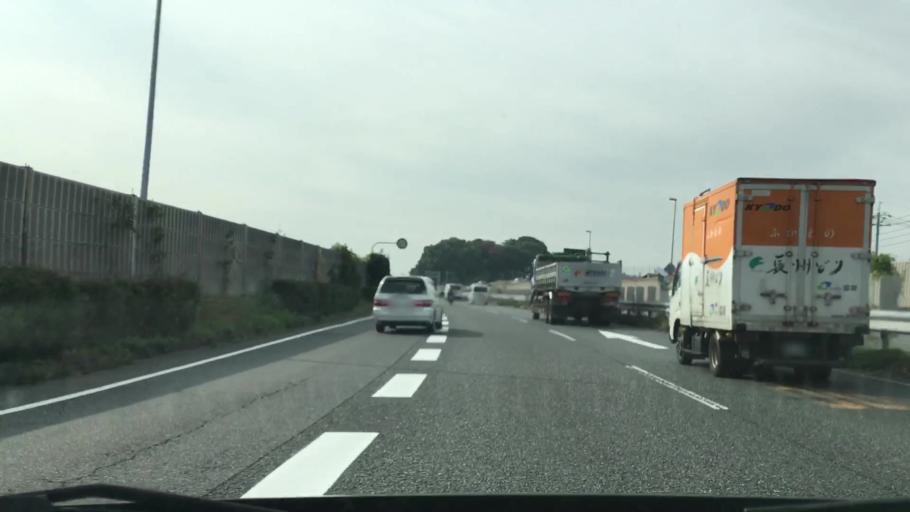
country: JP
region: Hiroshima
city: Hatsukaichi
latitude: 34.3812
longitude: 132.3502
